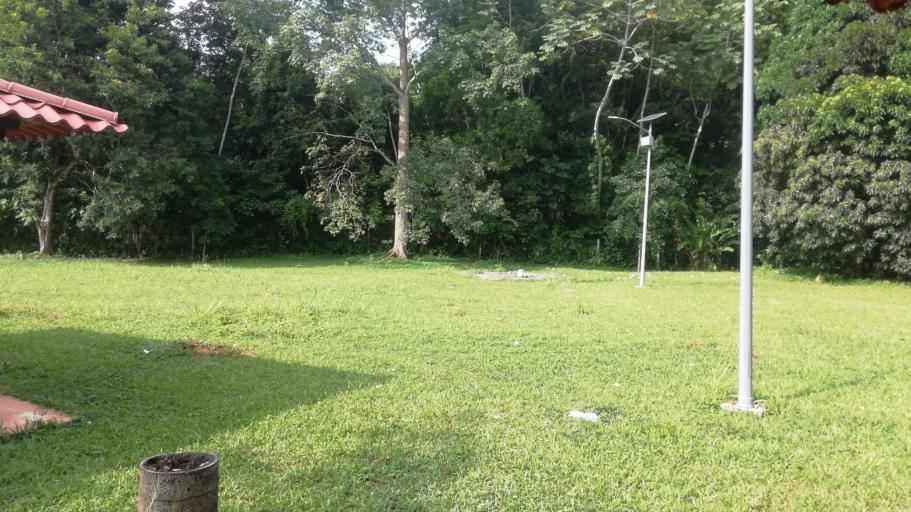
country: MX
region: Tabasco
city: Teapa
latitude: 17.5276
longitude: -92.9303
